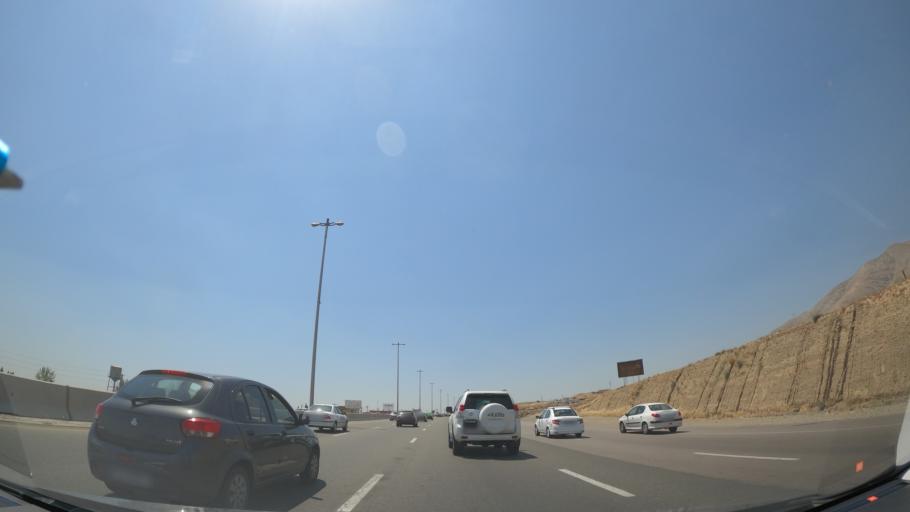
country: IR
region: Tehran
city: Shahr-e Qods
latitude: 35.7450
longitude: 51.0928
